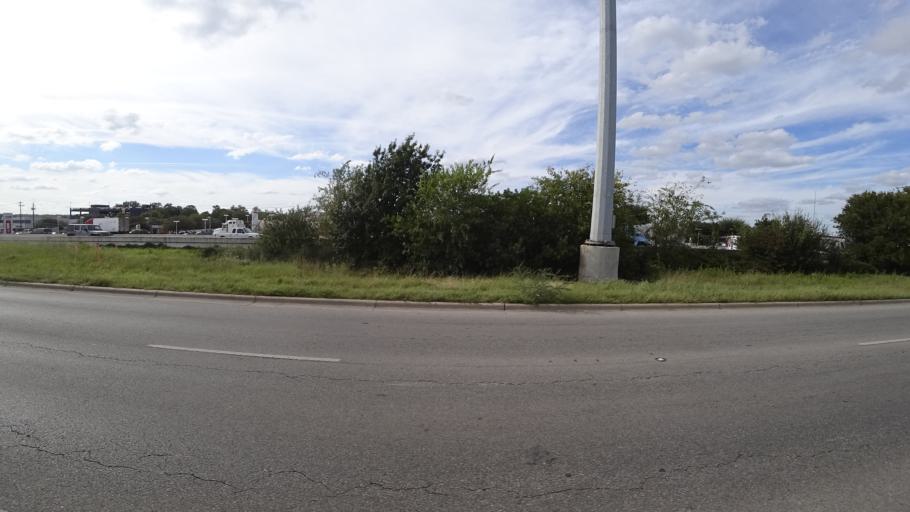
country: US
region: Texas
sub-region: Travis County
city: Austin
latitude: 30.2072
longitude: -97.7565
